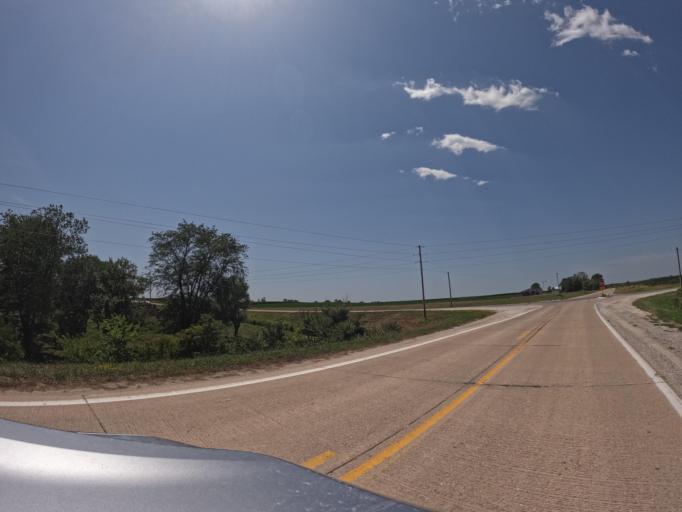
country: US
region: Iowa
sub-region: Henry County
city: Mount Pleasant
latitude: 40.9799
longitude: -91.6115
